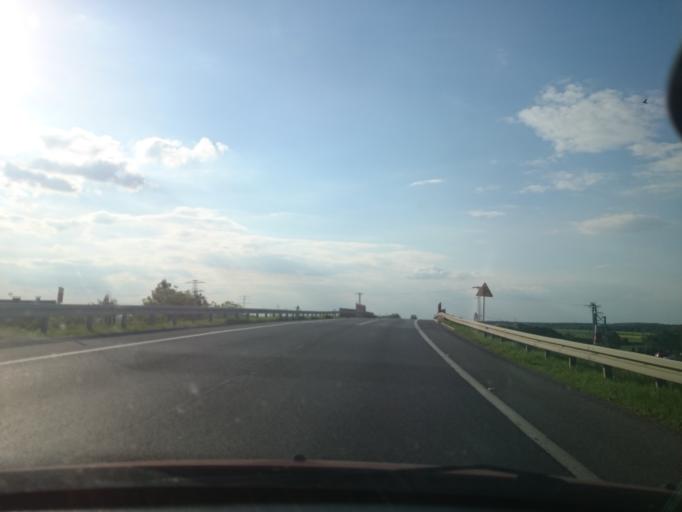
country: PL
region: Opole Voivodeship
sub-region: Powiat strzelecki
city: Strzelce Opolskie
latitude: 50.5217
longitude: 18.2789
